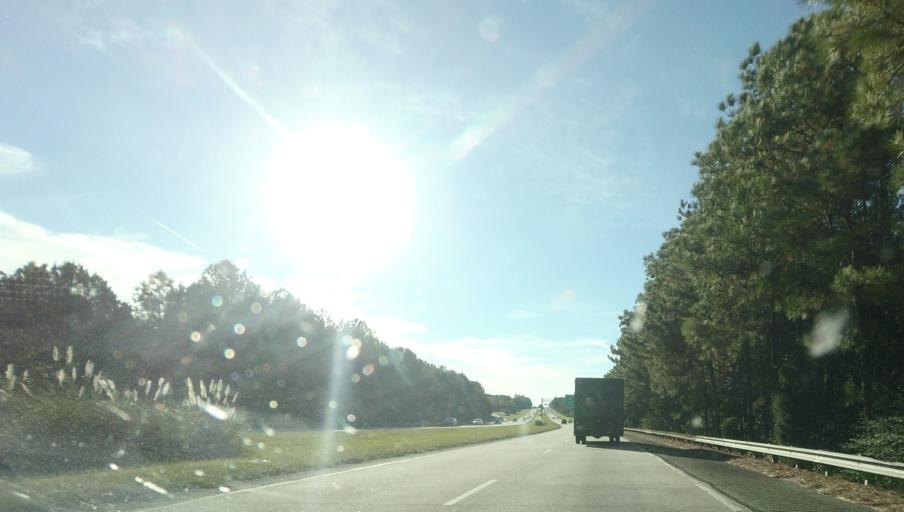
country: US
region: Georgia
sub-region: Muscogee County
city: Columbus
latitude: 32.5549
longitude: -84.9170
